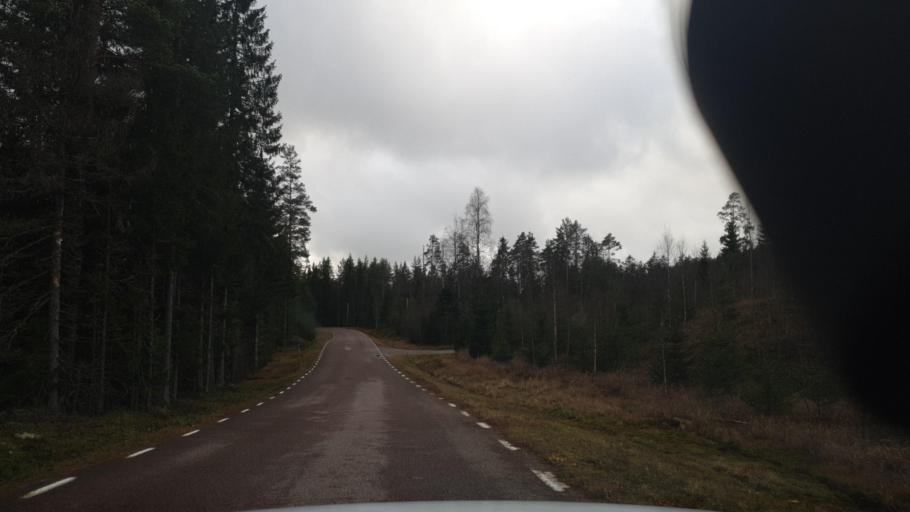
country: SE
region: Vaermland
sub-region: Arvika Kommun
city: Arvika
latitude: 59.8008
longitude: 12.8373
